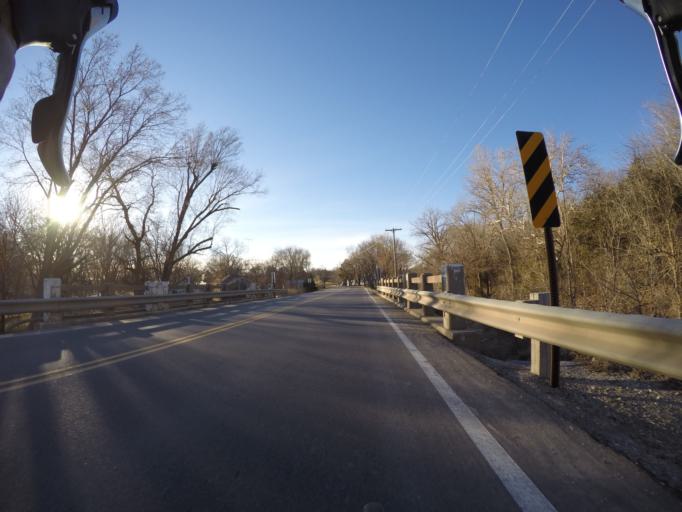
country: US
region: Kansas
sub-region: Riley County
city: Ogden
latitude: 39.2238
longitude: -96.7063
